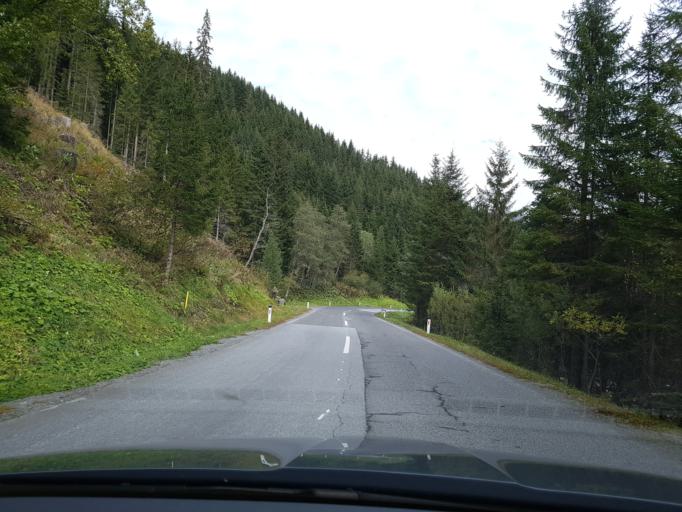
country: AT
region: Salzburg
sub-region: Politischer Bezirk Tamsweg
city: Ramingstein
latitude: 46.9686
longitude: 13.8914
